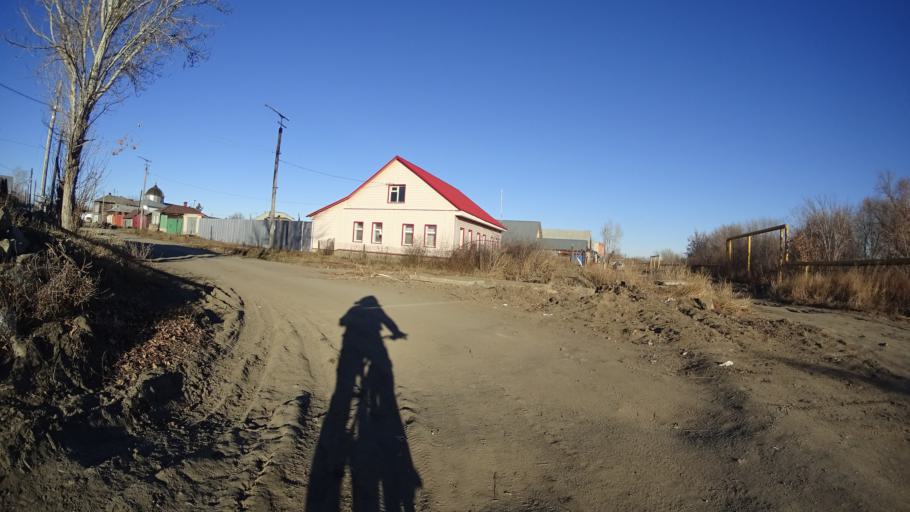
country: RU
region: Chelyabinsk
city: Troitsk
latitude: 54.0818
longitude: 61.5686
